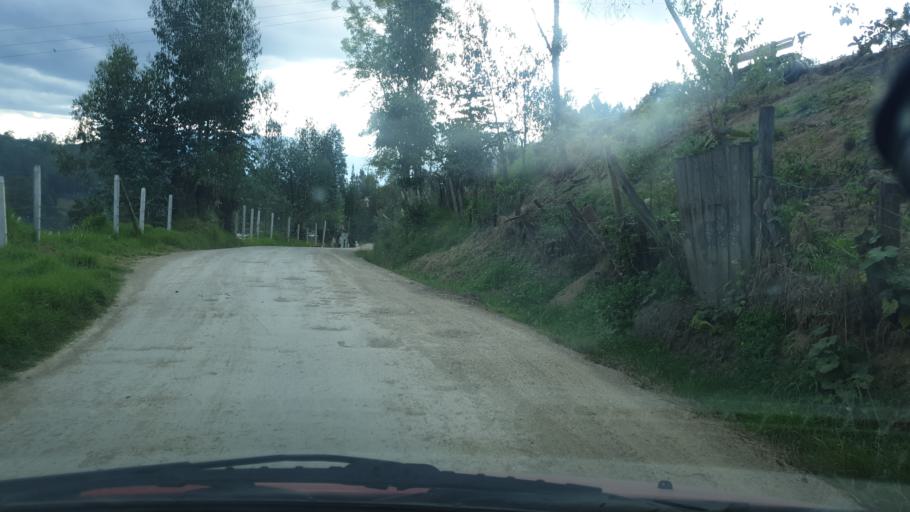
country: EC
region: Azuay
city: Cuenca
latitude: -2.9190
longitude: -78.9763
